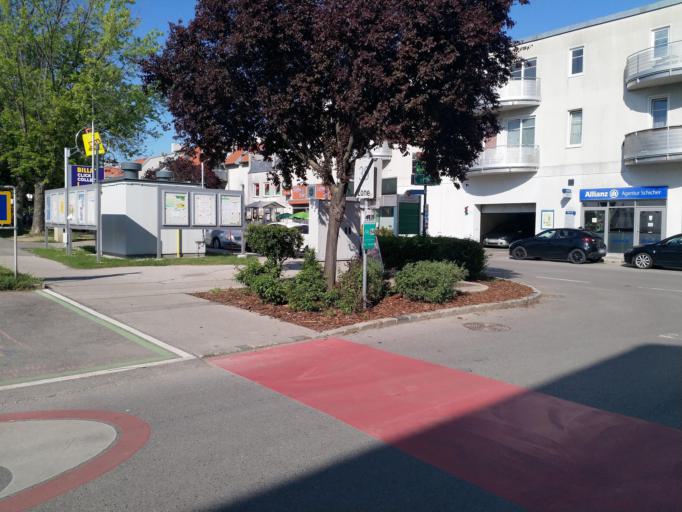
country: AT
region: Lower Austria
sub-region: Politischer Bezirk Wien-Umgebung
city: Leopoldsdorf
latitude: 48.1092
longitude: 16.3931
